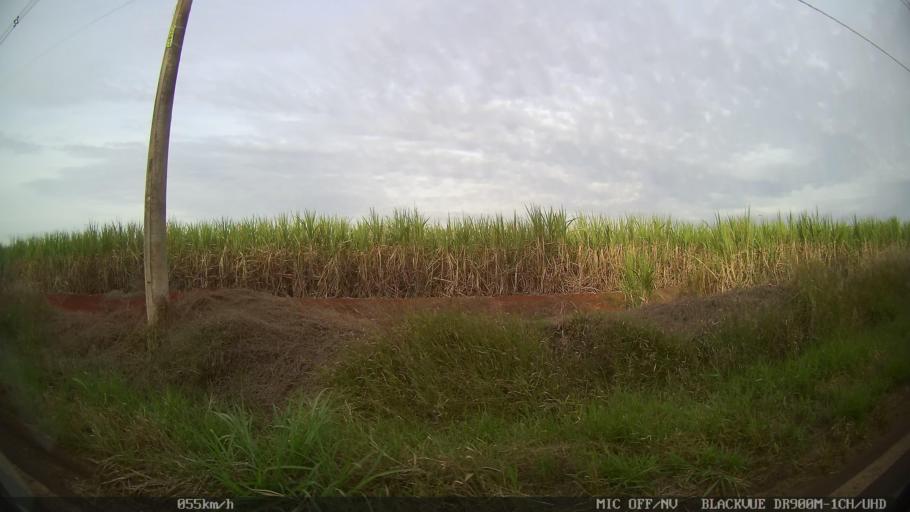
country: BR
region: Sao Paulo
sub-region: Piracicaba
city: Piracicaba
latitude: -22.7126
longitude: -47.5804
